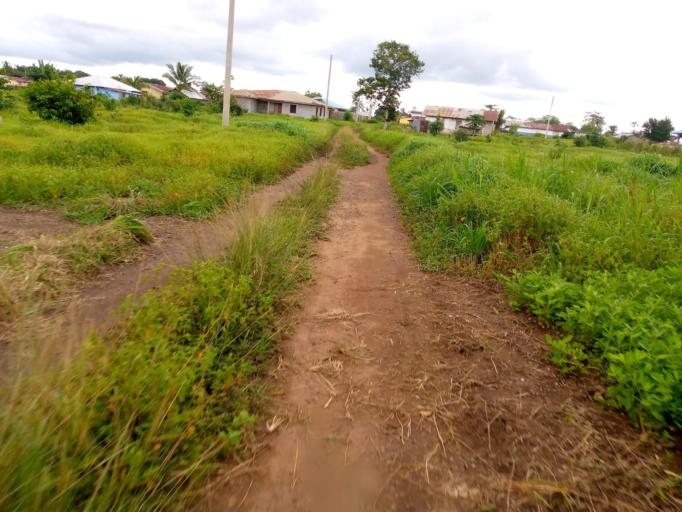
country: SL
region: Southern Province
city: Moyamba
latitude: 8.1528
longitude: -12.4400
